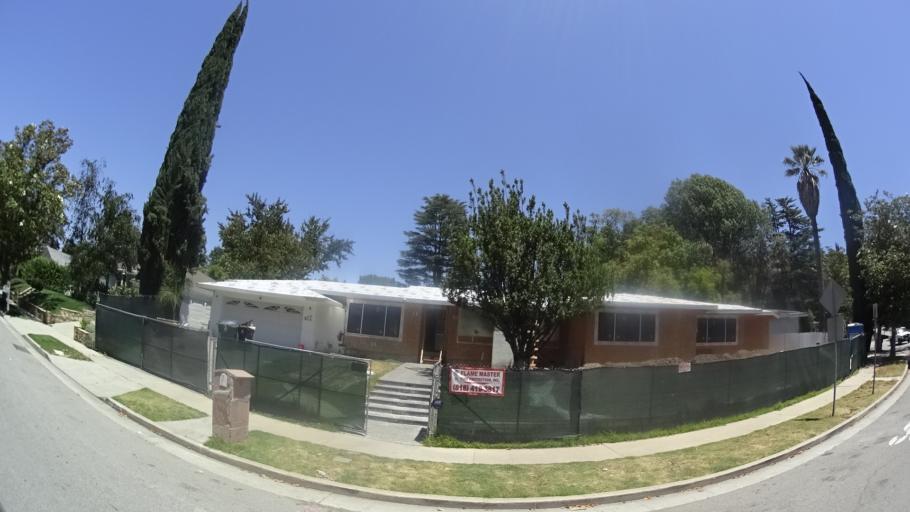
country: US
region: California
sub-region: Los Angeles County
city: Sherman Oaks
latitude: 34.1475
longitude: -118.4723
